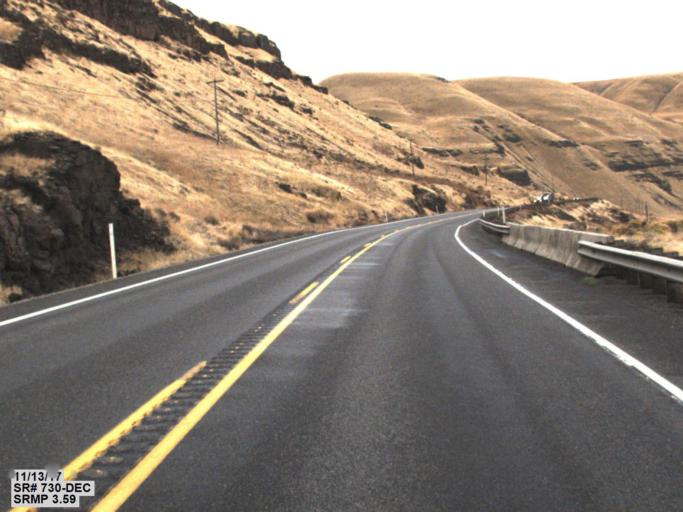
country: US
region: Washington
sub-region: Benton County
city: Finley
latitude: 46.0377
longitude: -118.9374
